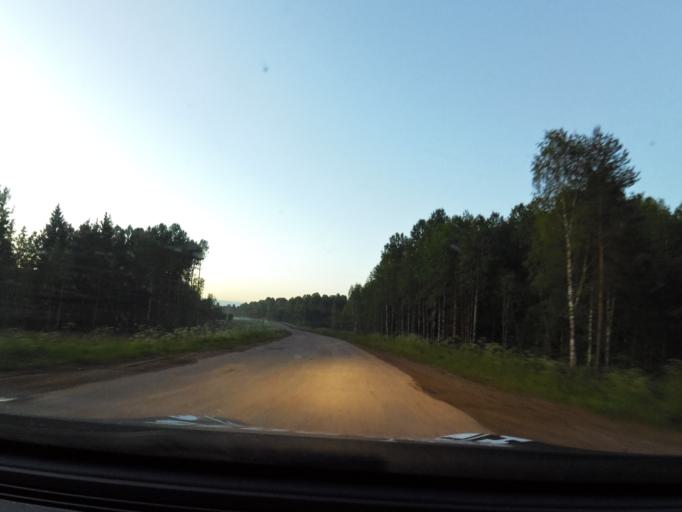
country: RU
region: Vologda
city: Vytegra
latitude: 60.9932
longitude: 36.3696
